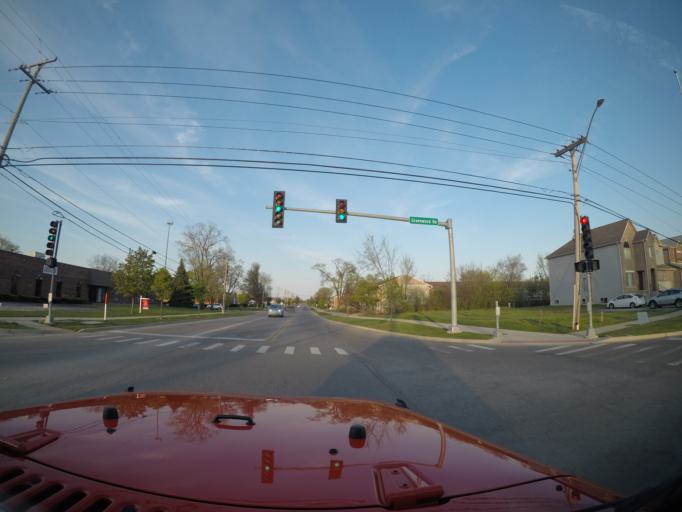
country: US
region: Illinois
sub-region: Cook County
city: Northbrook
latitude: 42.0875
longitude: -87.8394
